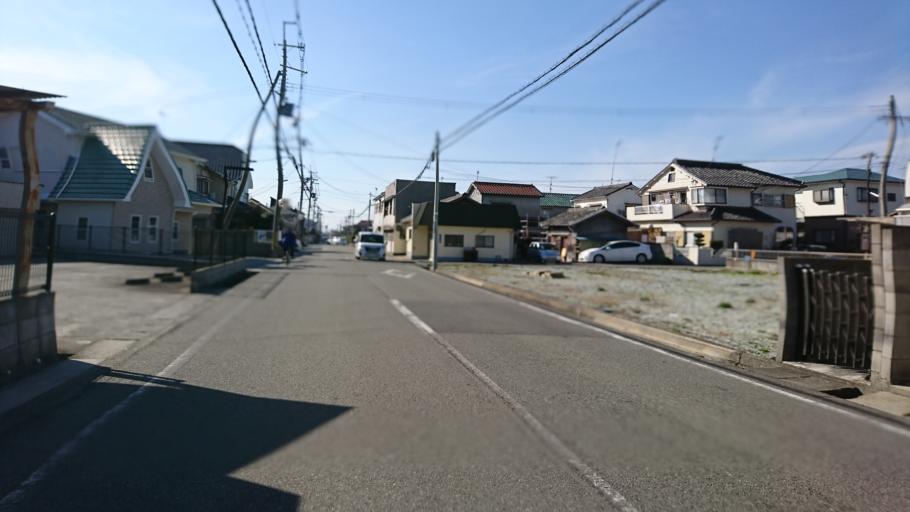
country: JP
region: Hyogo
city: Kakogawacho-honmachi
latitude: 34.7224
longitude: 134.8840
